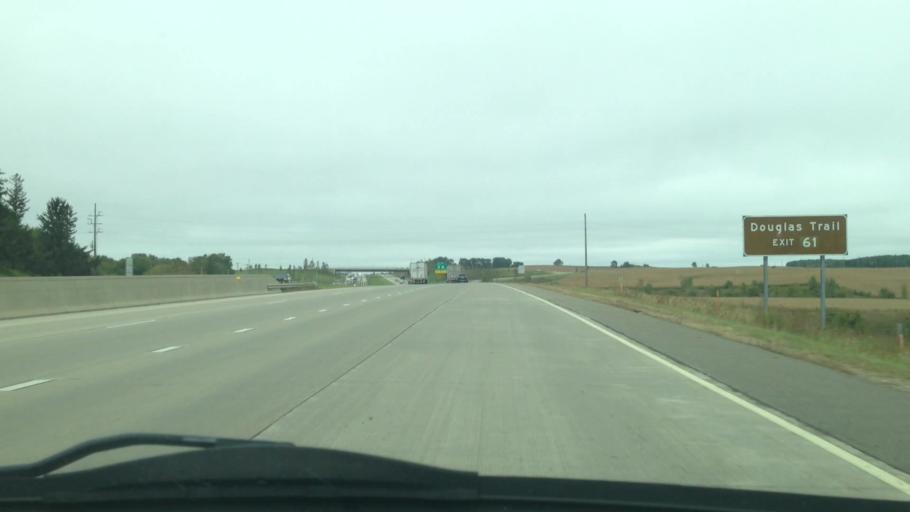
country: US
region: Minnesota
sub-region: Olmsted County
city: Oronoco
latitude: 44.0991
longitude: -92.5123
